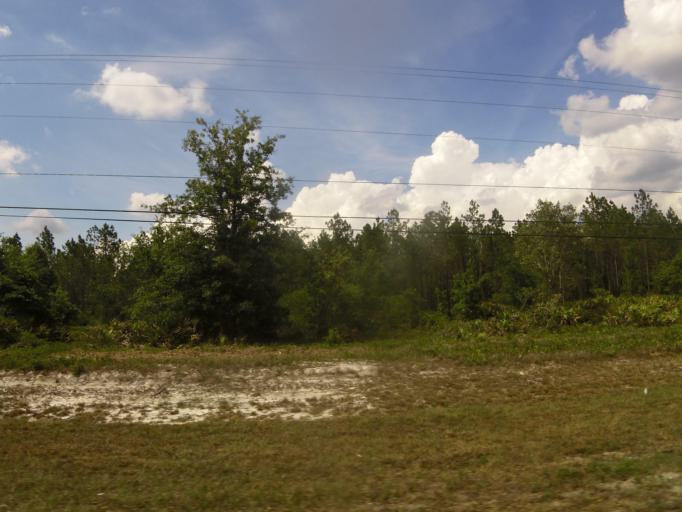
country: US
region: Florida
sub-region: Baker County
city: Macclenny
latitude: 30.2013
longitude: -82.0391
